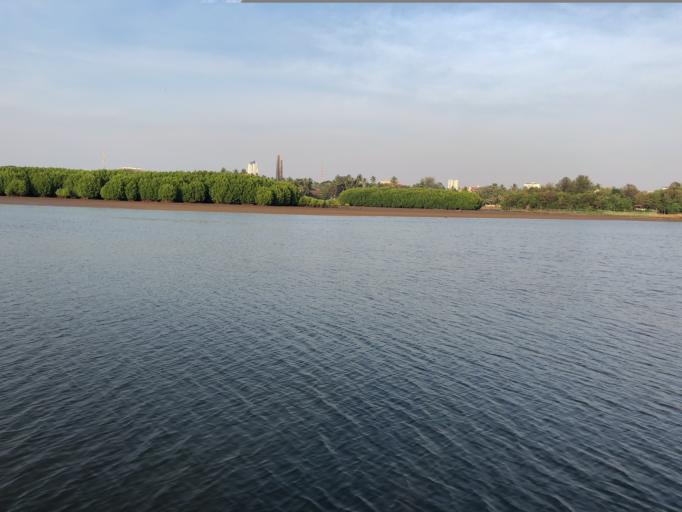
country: IN
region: Karnataka
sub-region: Dakshina Kannada
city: Mangalore
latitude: 12.8769
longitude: 74.8234
